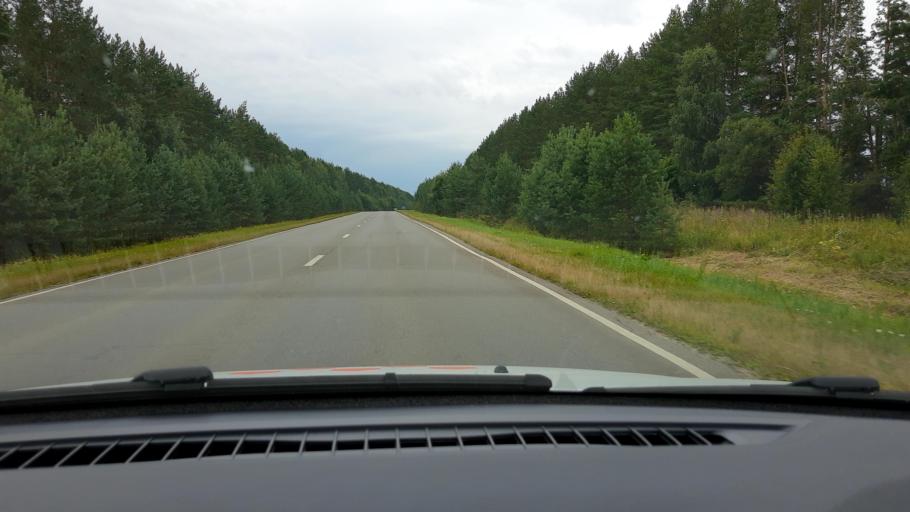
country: RU
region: Nizjnij Novgorod
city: Vyyezdnoye
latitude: 55.1688
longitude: 43.5922
